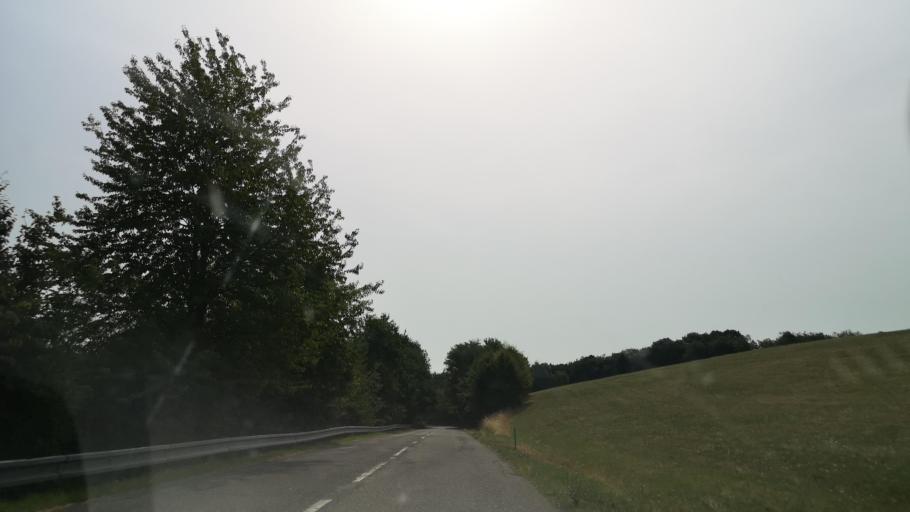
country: SK
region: Banskobystricky
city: Revuca
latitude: 48.5842
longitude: 20.0661
